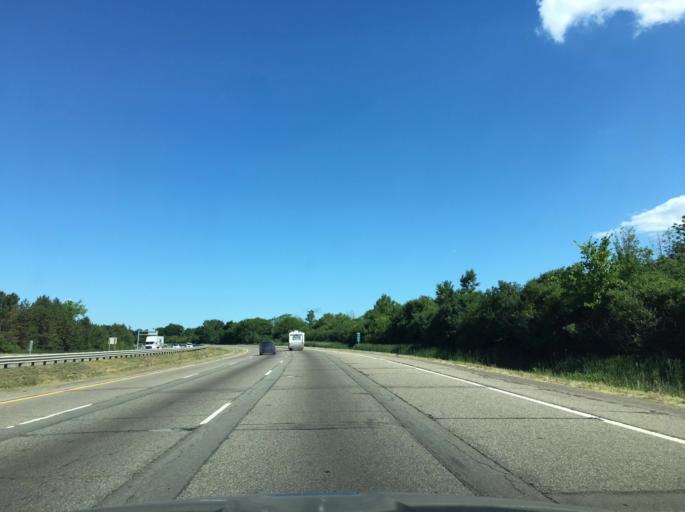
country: US
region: Michigan
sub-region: Oakland County
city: Troy
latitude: 42.6005
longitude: -83.1631
